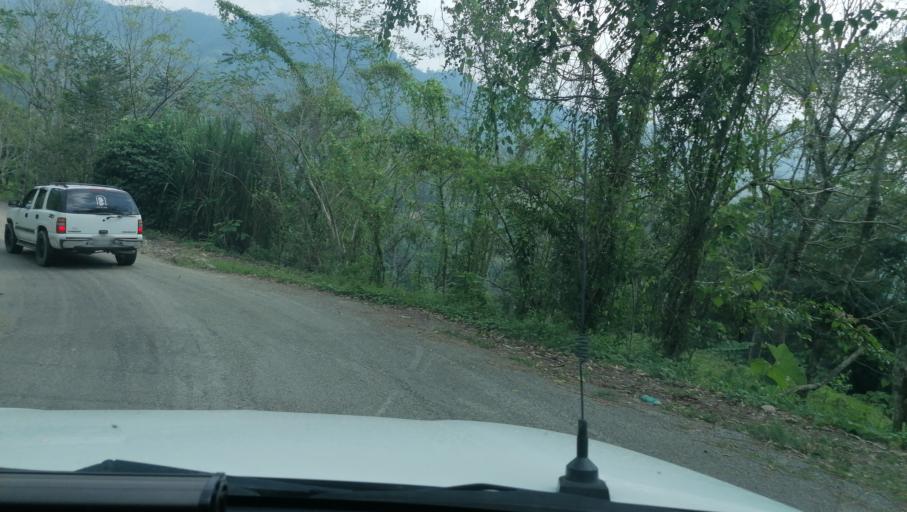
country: MX
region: Chiapas
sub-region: Francisco Leon
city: San Miguel la Sardina
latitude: 17.2249
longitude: -93.3462
